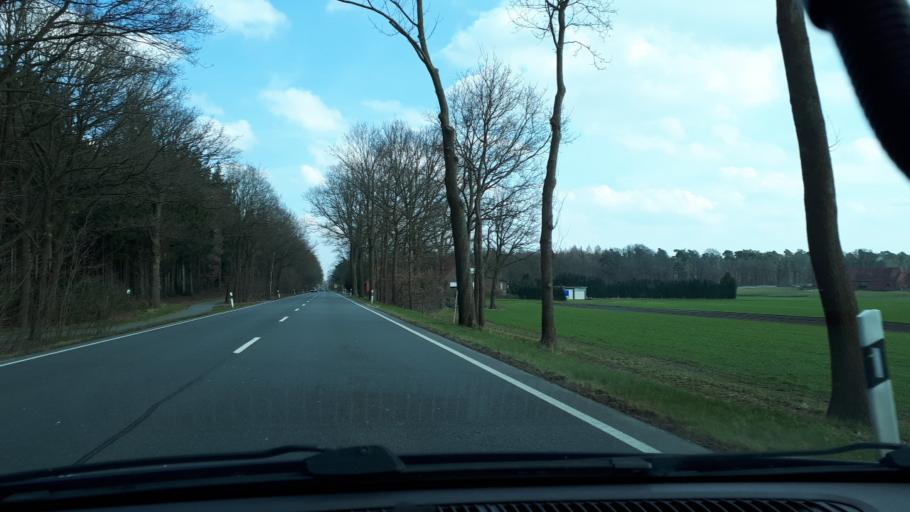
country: DE
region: Lower Saxony
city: Pennigsehl
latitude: 52.6626
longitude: 9.0447
